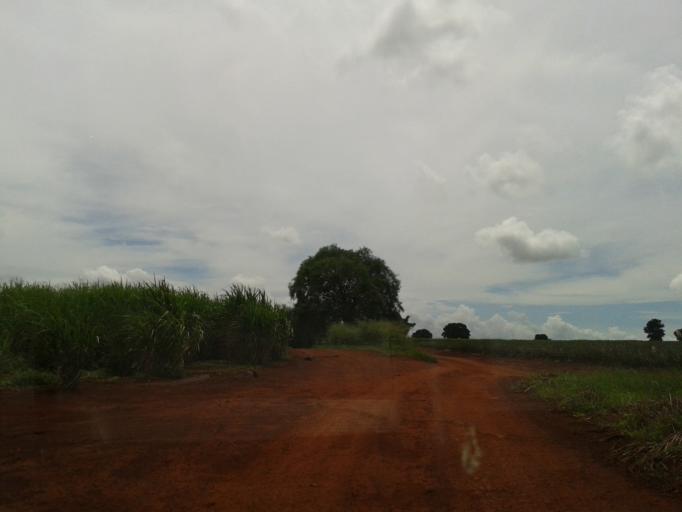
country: BR
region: Minas Gerais
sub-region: Centralina
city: Centralina
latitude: -18.5875
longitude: -49.2692
